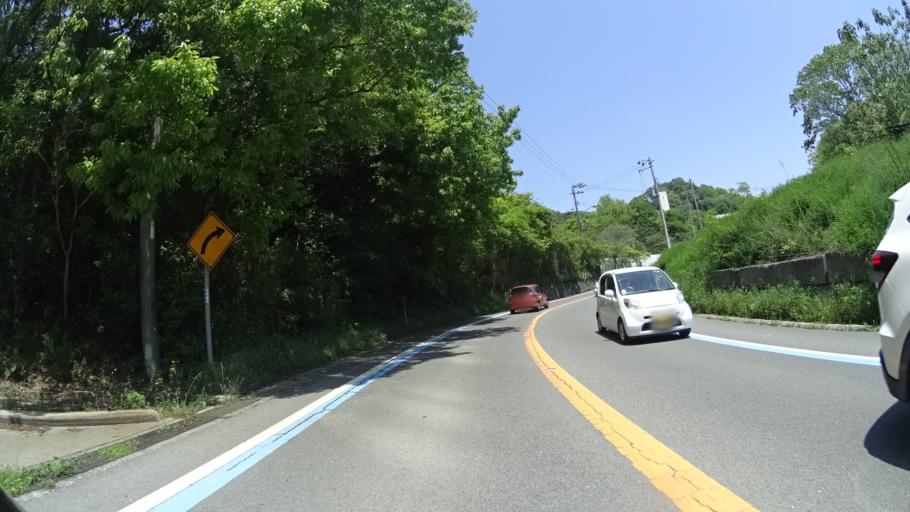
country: JP
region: Ehime
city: Iyo
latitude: 33.7136
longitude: 132.6677
